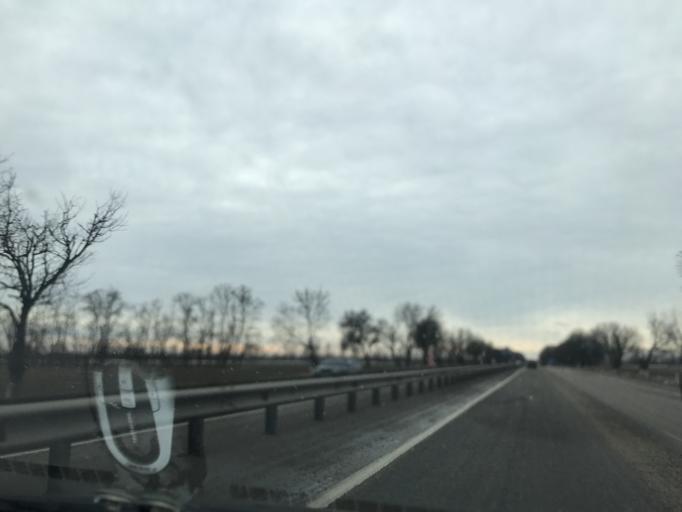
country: RU
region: Krasnodarskiy
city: Novokubansk
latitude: 45.0474
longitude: 40.9946
